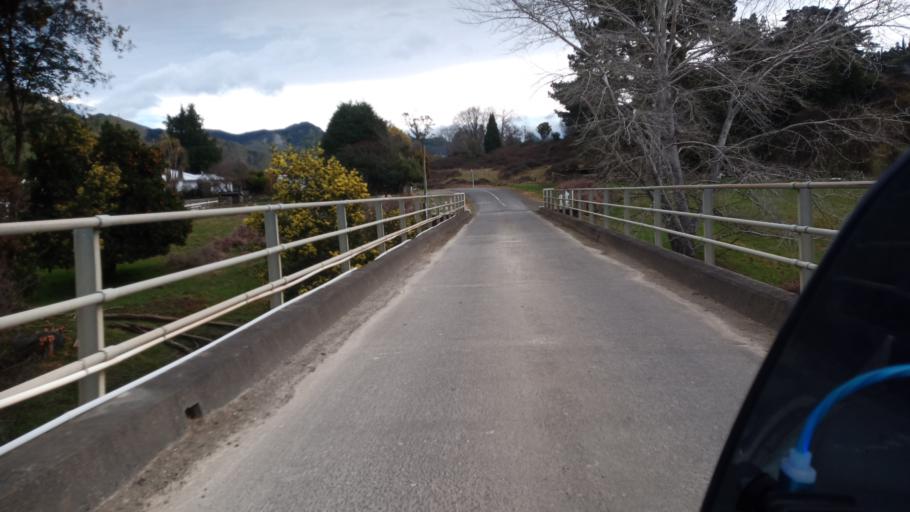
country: NZ
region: Hawke's Bay
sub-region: Wairoa District
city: Wairoa
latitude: -38.7683
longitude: 177.4051
